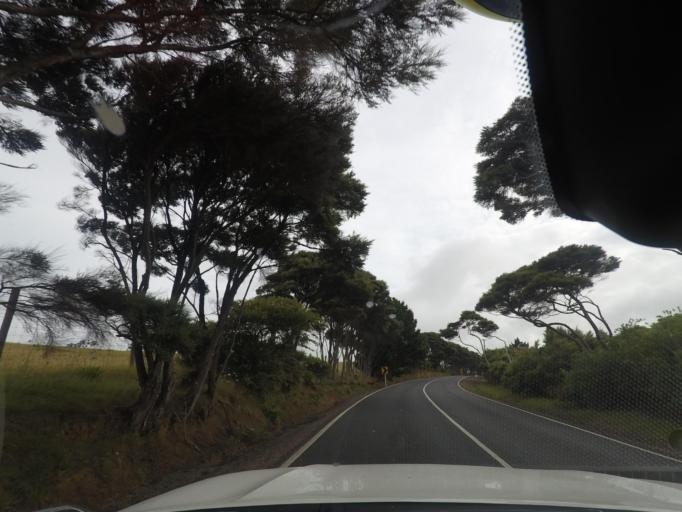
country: NZ
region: Auckland
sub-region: Auckland
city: Parakai
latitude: -36.4964
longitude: 174.2471
